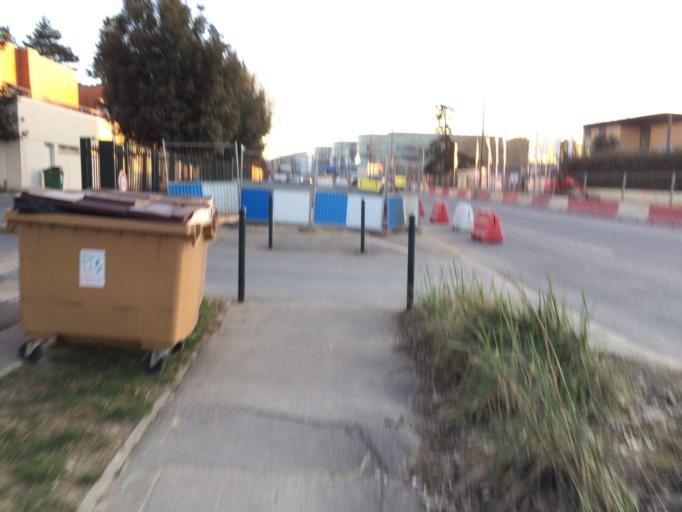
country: FR
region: Ile-de-France
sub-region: Departement des Hauts-de-Seine
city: Chatenay-Malabry
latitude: 48.7782
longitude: 2.2508
